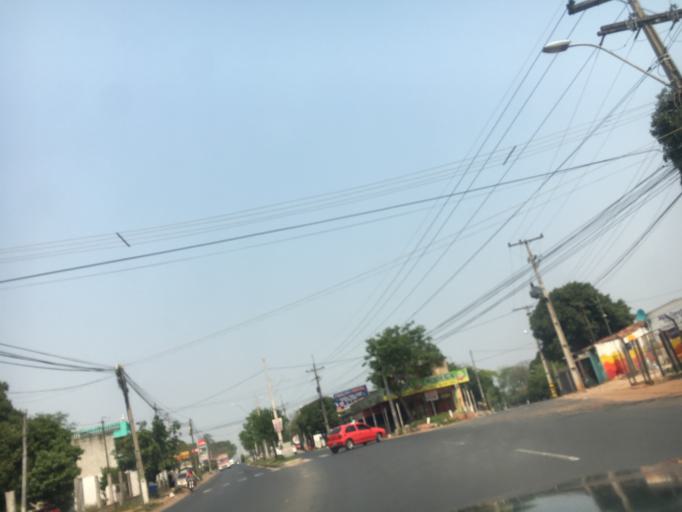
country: PY
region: Central
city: Villa Elisa
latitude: -25.3821
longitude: -57.5850
